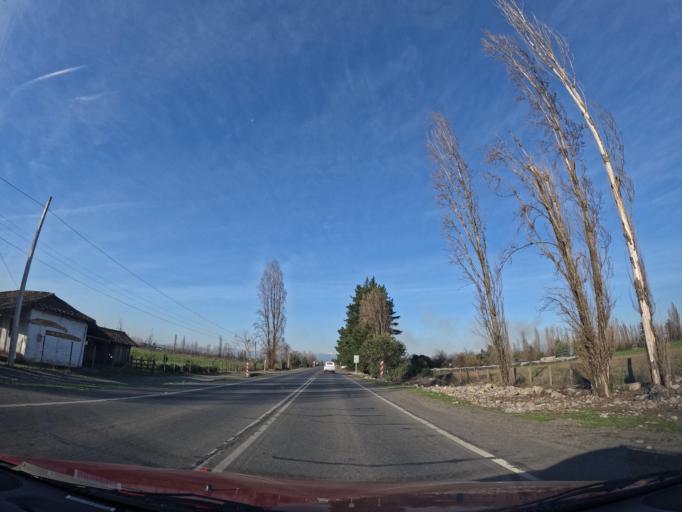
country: CL
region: Maule
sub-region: Provincia de Talca
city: San Clemente
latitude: -35.6271
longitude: -71.4746
